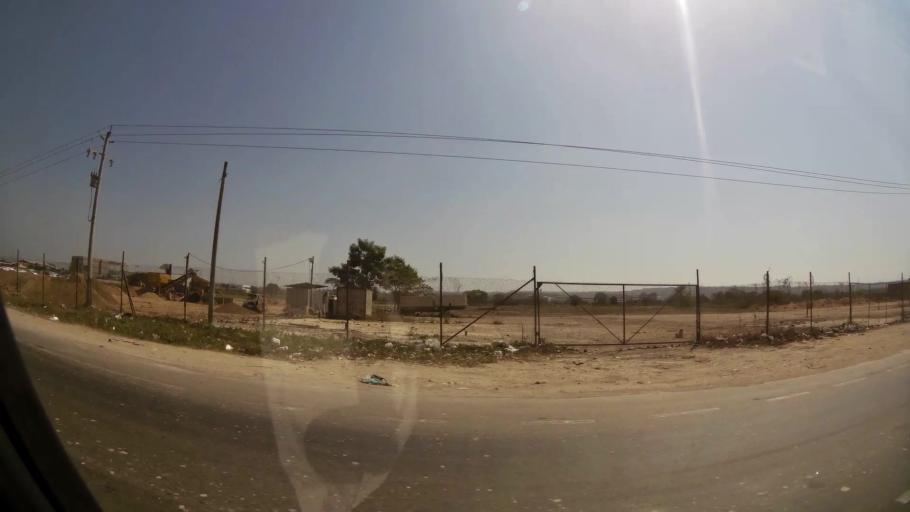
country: CO
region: Bolivar
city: Cartagena
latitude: 10.3863
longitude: -75.4497
